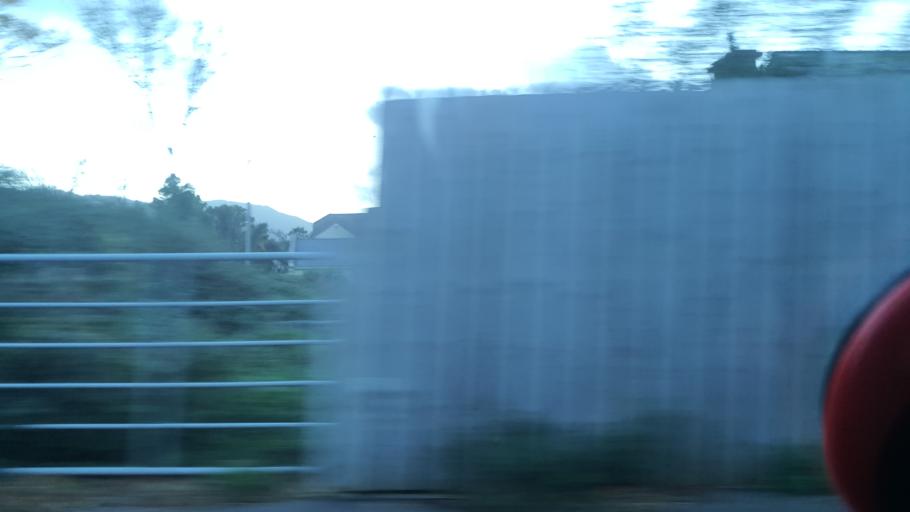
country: GB
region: Northern Ireland
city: Rostrevor
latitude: 54.0781
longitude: -6.1829
